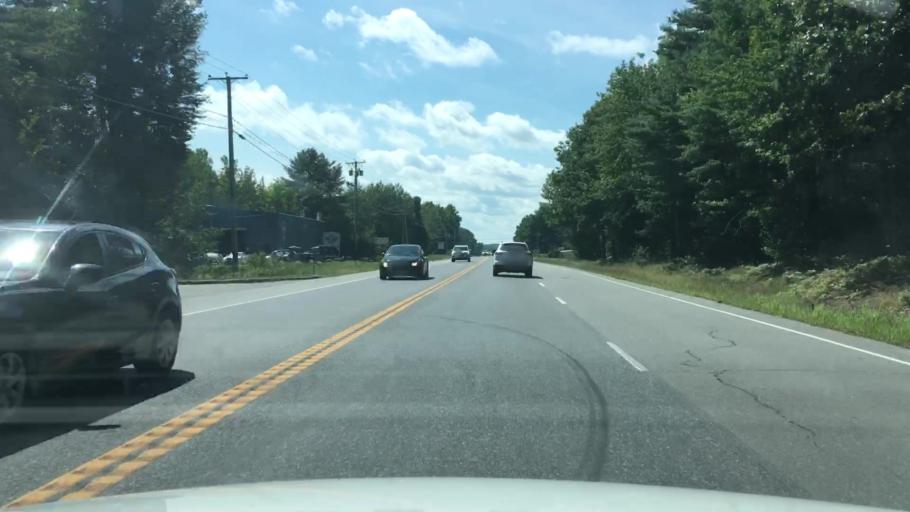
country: US
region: Maine
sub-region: Kennebec County
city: Winthrop
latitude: 44.2871
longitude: -69.9972
